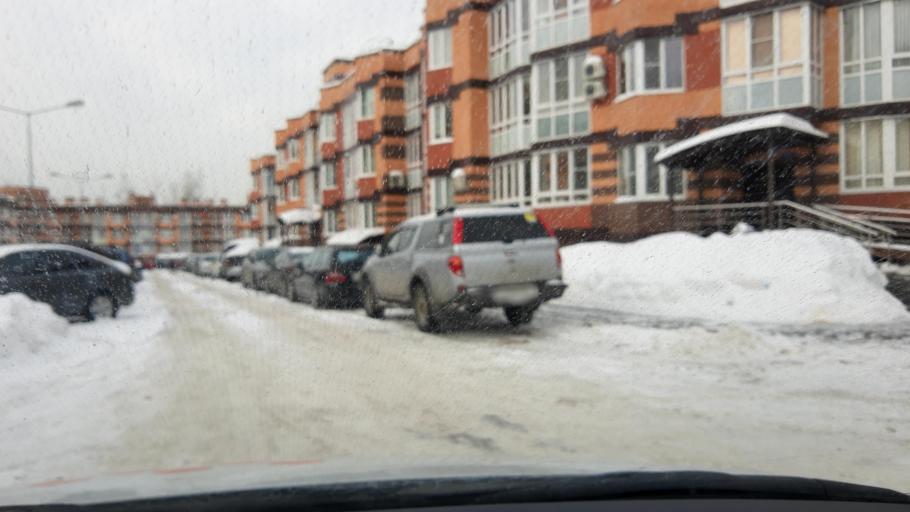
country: RU
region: Moskovskaya
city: Kommunarka
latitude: 55.5496
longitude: 37.4986
